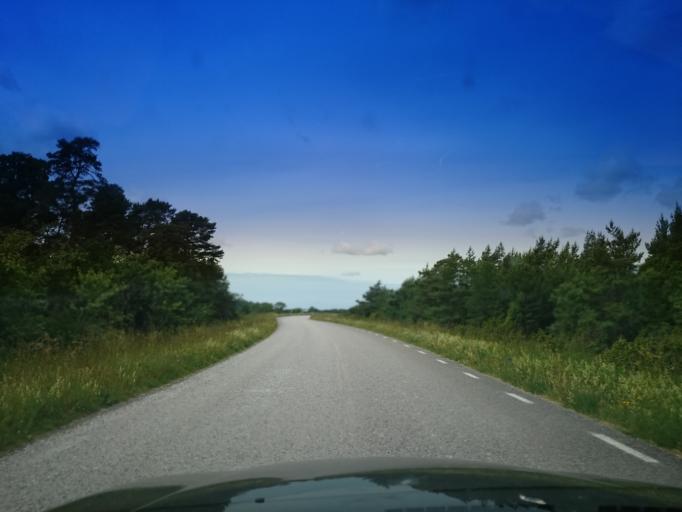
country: SE
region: Gotland
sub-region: Gotland
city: Hemse
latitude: 57.2528
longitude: 18.5868
